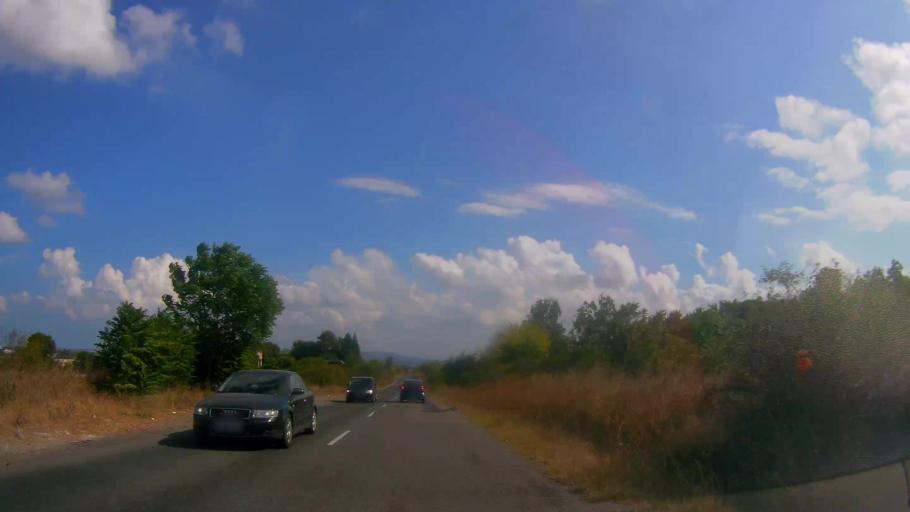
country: BG
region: Burgas
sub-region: Obshtina Burgas
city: Burgas
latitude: 42.4755
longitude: 27.4163
